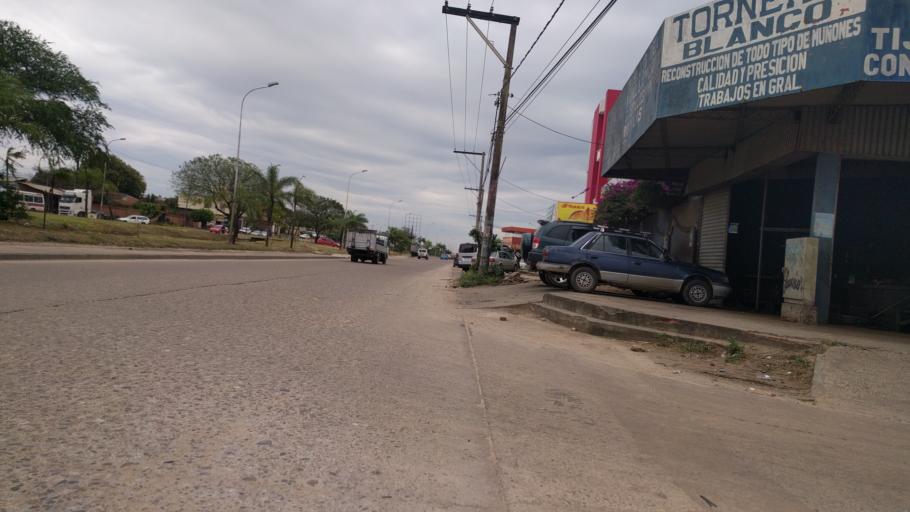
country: BO
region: Santa Cruz
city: Santa Cruz de la Sierra
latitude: -17.8186
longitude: -63.1988
